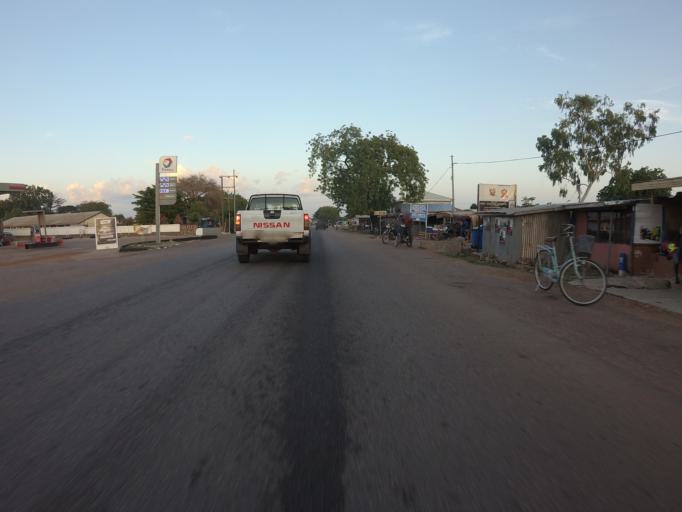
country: GH
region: Upper East
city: Navrongo
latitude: 10.8952
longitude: -1.0841
